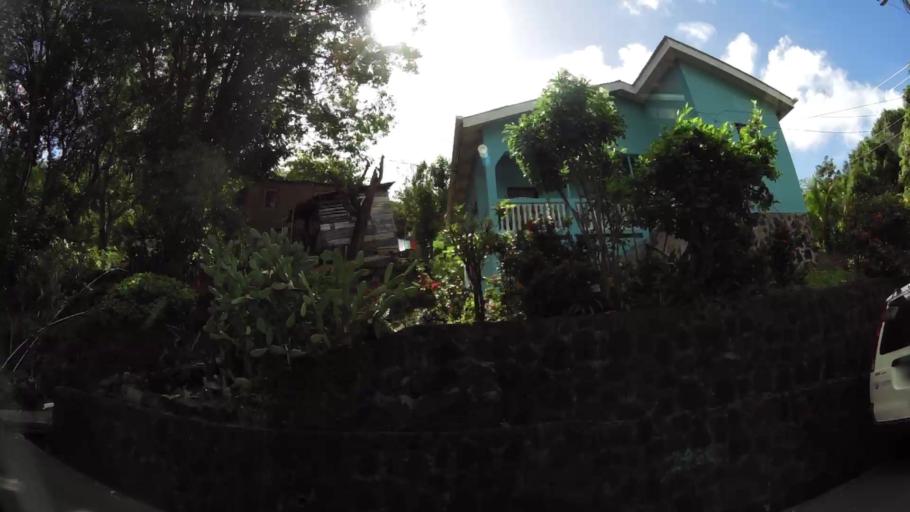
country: LC
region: Laborie Quarter
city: Laborie
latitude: 13.7509
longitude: -60.9921
